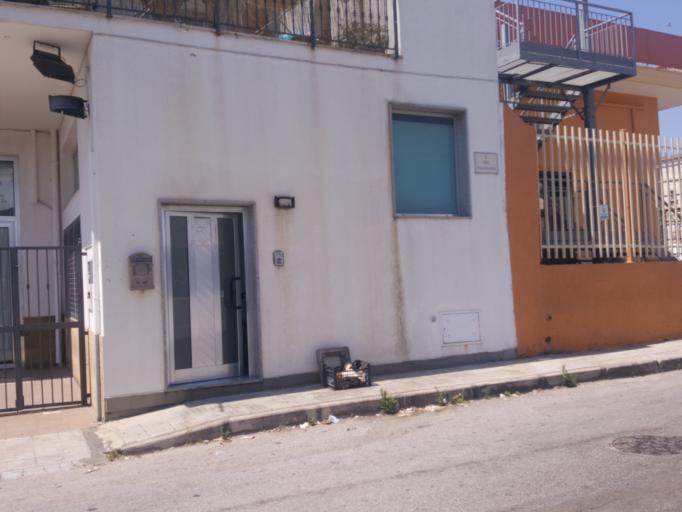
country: IT
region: Apulia
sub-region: Provincia di Taranto
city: Massafra
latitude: 40.5850
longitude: 17.1084
